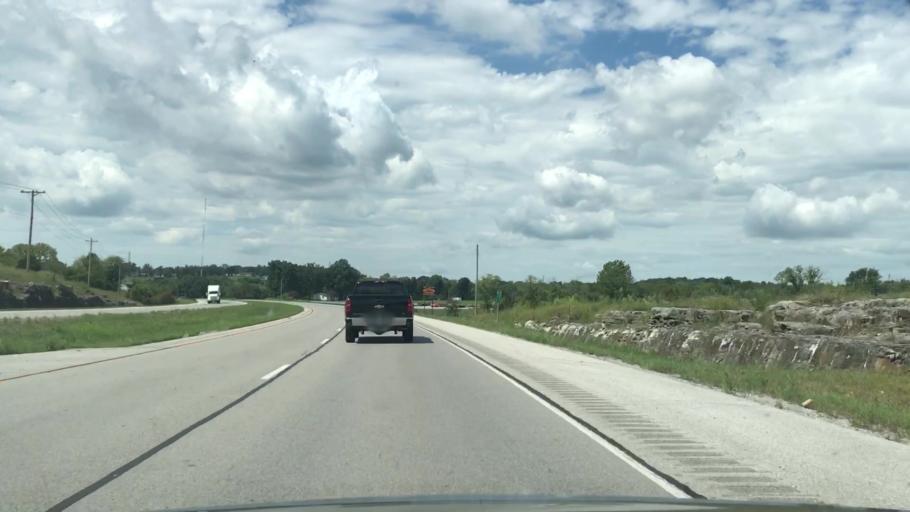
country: US
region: Kentucky
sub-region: Logan County
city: Russellville
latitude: 36.8669
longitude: -86.8934
